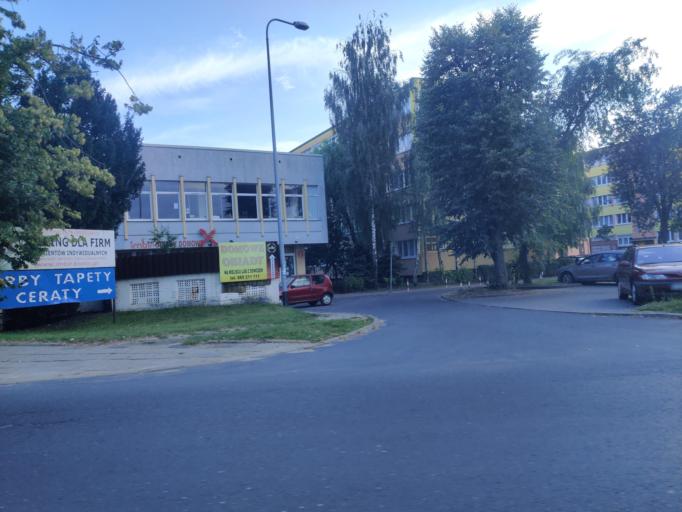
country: PL
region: Greater Poland Voivodeship
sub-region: Konin
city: Konin
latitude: 52.2306
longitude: 18.2690
